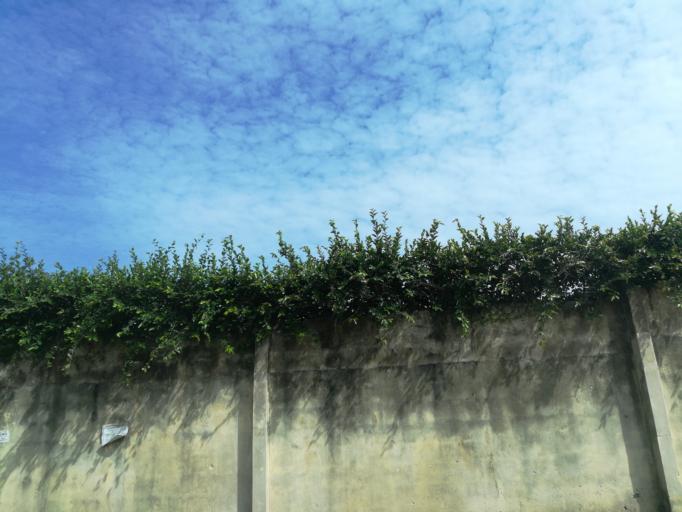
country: NG
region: Lagos
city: Ojota
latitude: 6.5780
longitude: 3.3646
